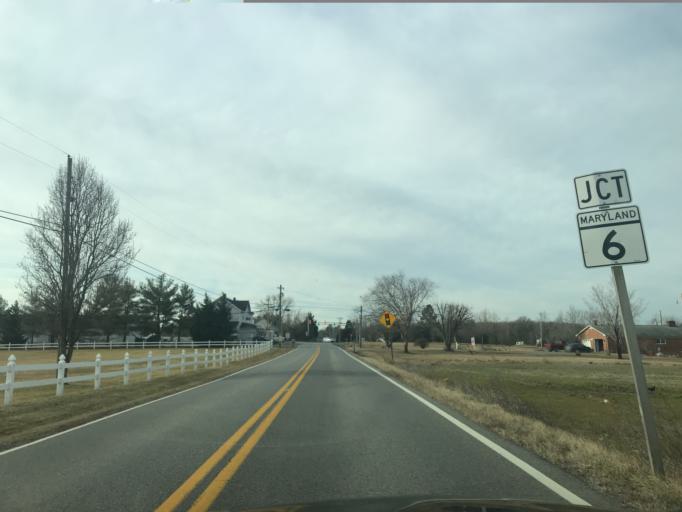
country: US
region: Maryland
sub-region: Charles County
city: La Plata
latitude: 38.4832
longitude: -76.8915
